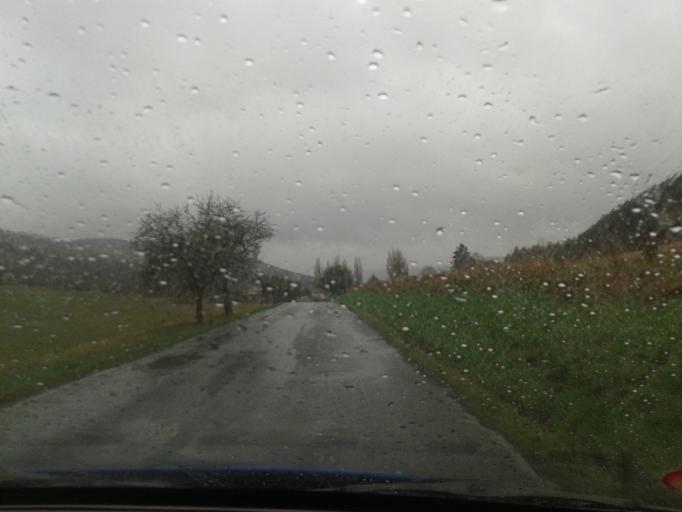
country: CZ
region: Central Bohemia
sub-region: Okres Beroun
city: Kraluv Dvur
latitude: 49.9159
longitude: 14.0254
